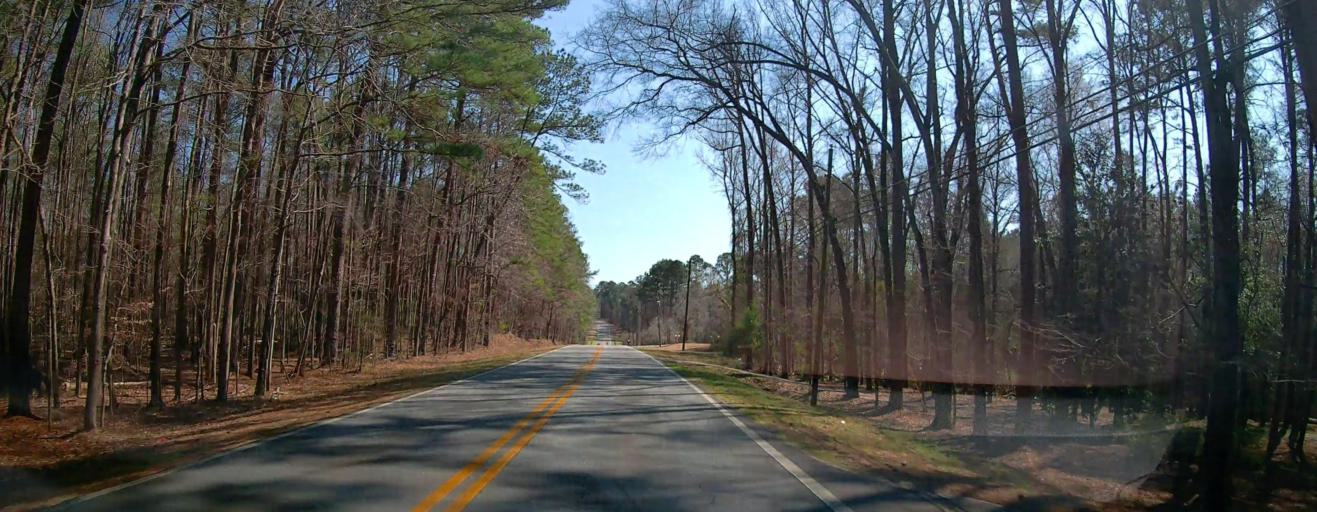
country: US
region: Georgia
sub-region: Bibb County
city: Macon
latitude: 32.8951
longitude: -83.5893
